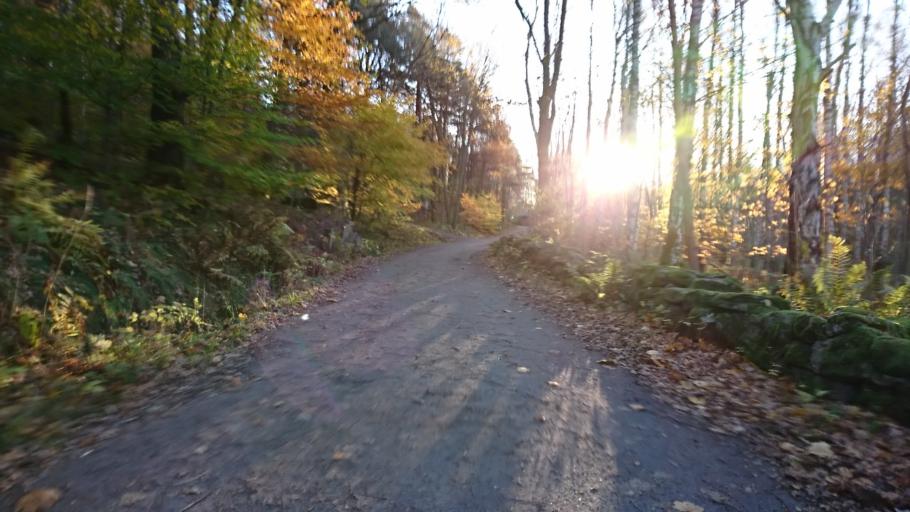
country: SE
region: Vaestra Goetaland
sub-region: Molndal
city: Moelndal
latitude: 57.6914
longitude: 12.0296
